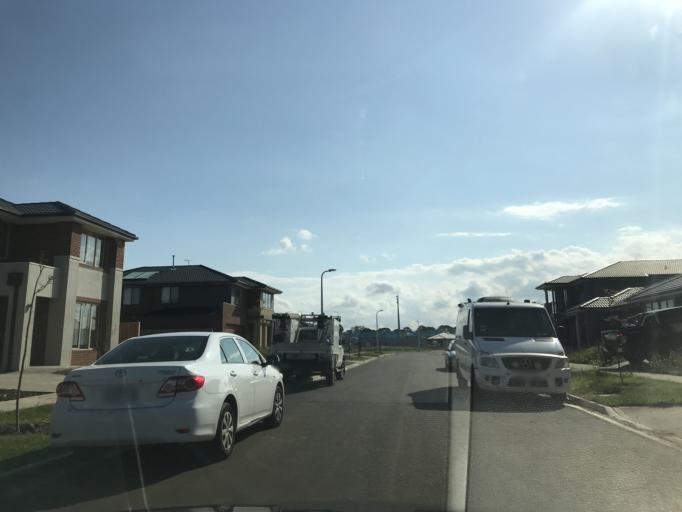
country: AU
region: Victoria
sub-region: Wyndham
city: Hoppers Crossing
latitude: -37.8910
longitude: 144.7129
